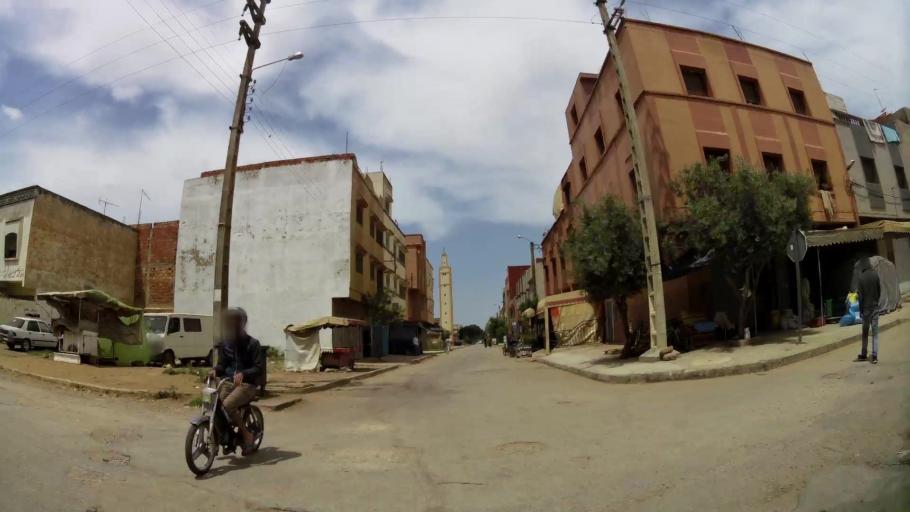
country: MA
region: Rabat-Sale-Zemmour-Zaer
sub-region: Khemisset
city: Khemisset
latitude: 33.8152
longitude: -6.0707
